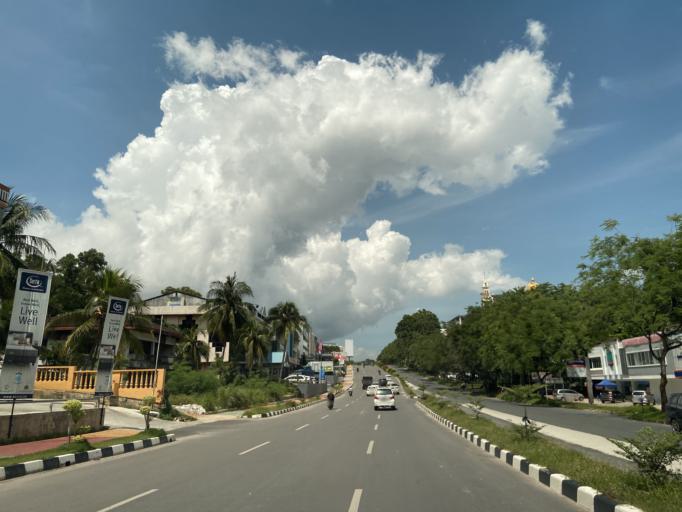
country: SG
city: Singapore
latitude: 1.1379
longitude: 104.0164
